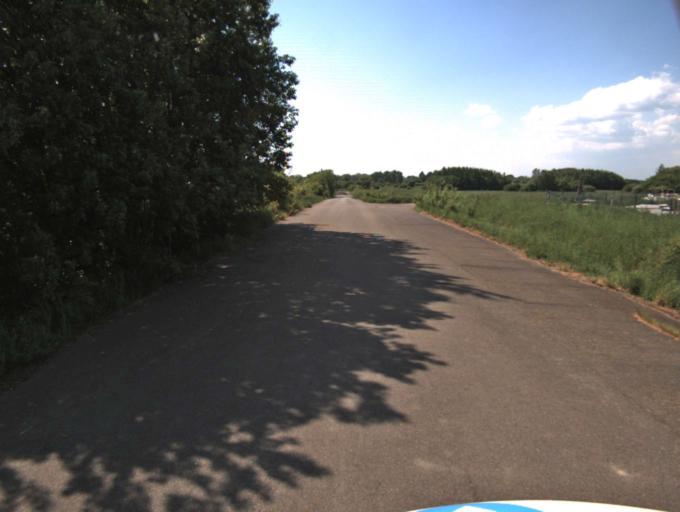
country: SE
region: Skane
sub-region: Kristianstads Kommun
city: Kristianstad
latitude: 56.0627
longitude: 14.1556
